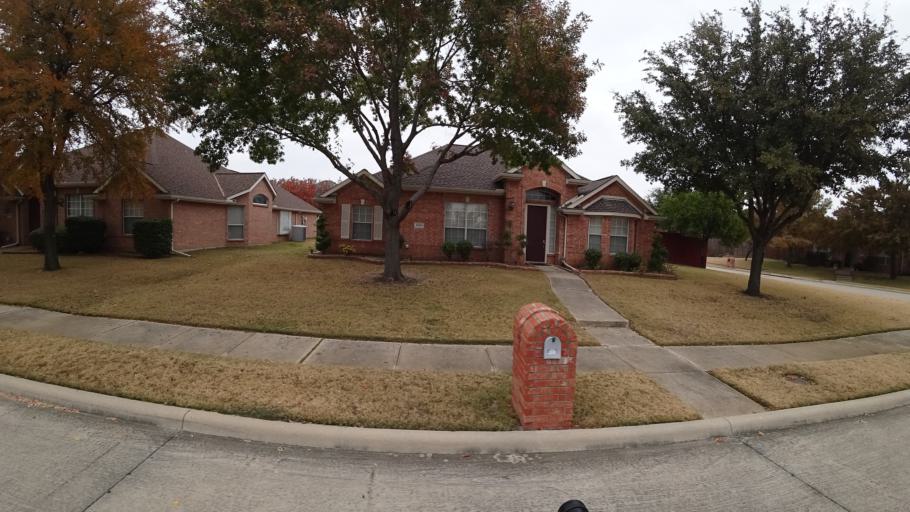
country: US
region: Texas
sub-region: Denton County
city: Lewisville
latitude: 33.0196
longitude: -96.9390
